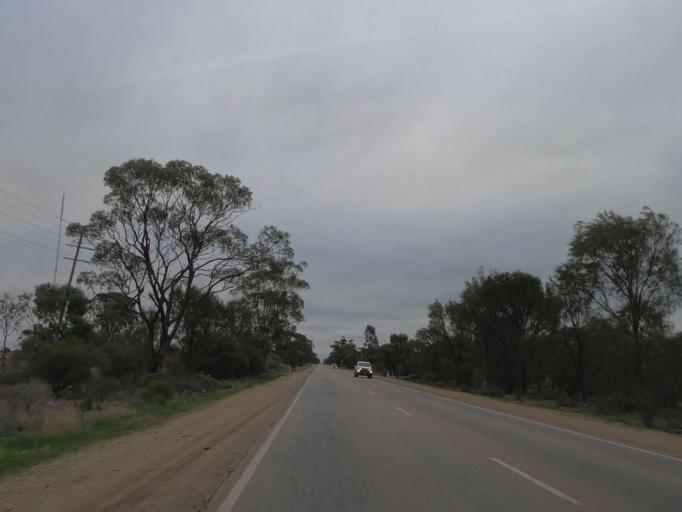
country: AU
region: Victoria
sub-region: Swan Hill
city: Swan Hill
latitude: -35.4097
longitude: 143.5845
